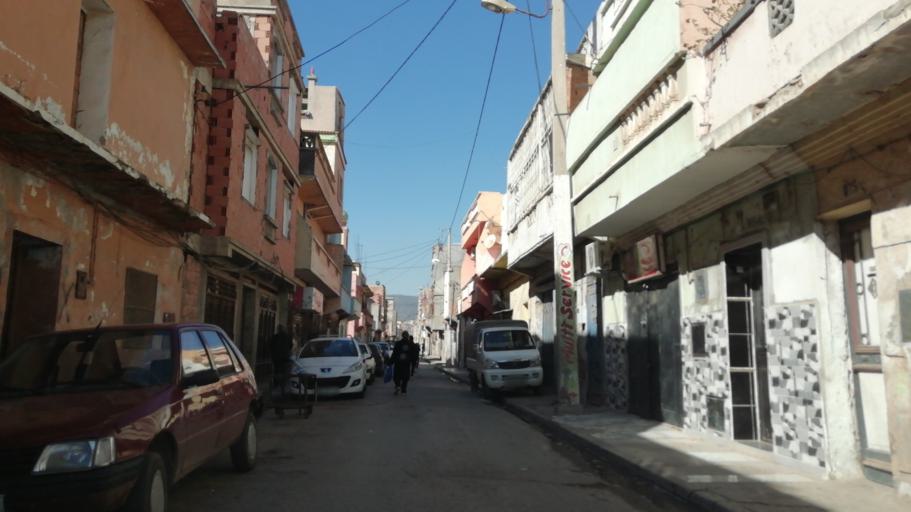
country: DZ
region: Oran
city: Oran
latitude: 35.6886
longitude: -0.6357
